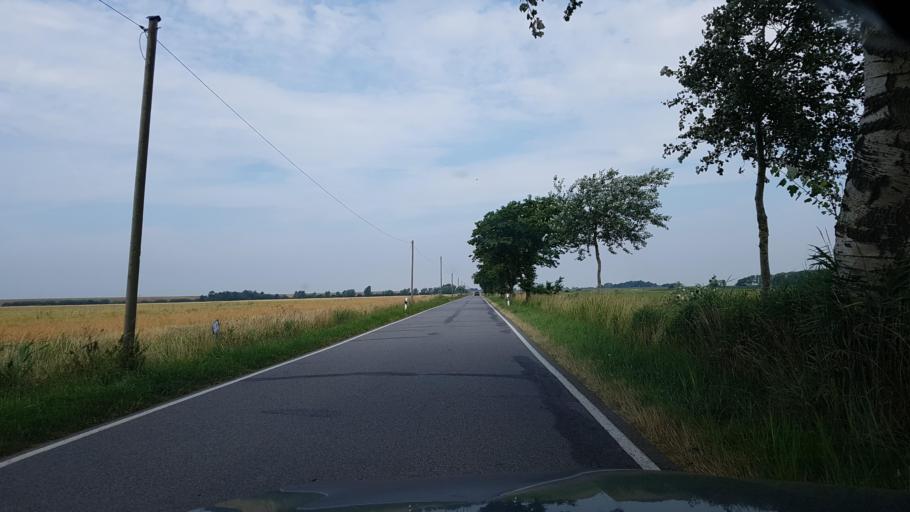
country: DE
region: Schleswig-Holstein
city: Tumlauer Koog
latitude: 54.3691
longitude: 8.7055
